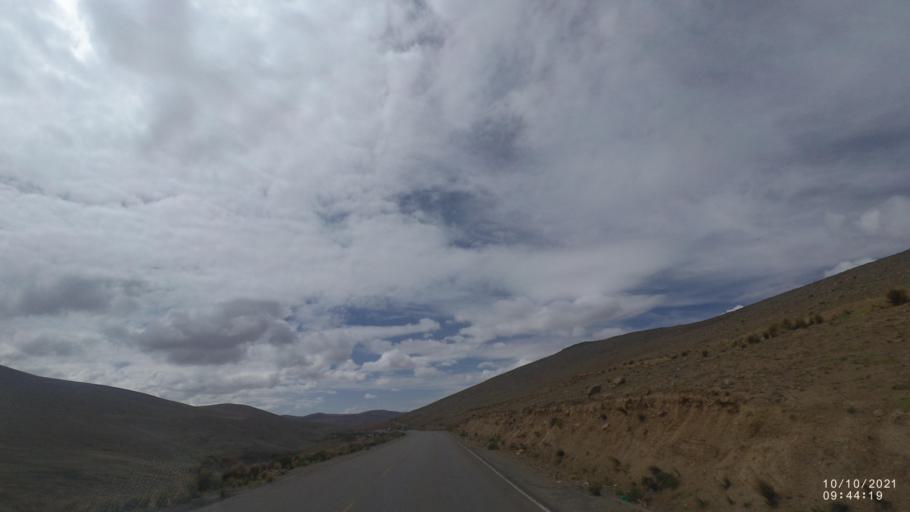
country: BO
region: La Paz
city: Quime
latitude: -17.1590
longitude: -67.3390
